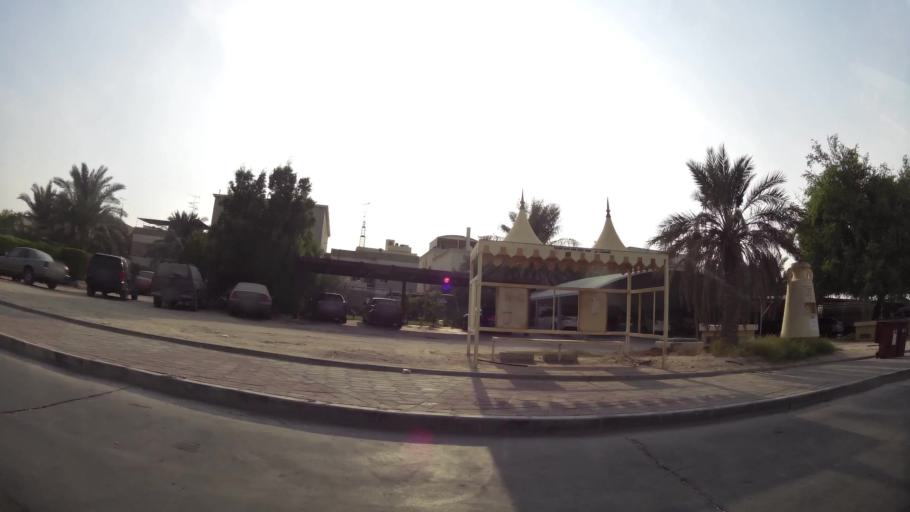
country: KW
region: Mubarak al Kabir
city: Sabah as Salim
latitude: 29.2540
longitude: 48.0552
